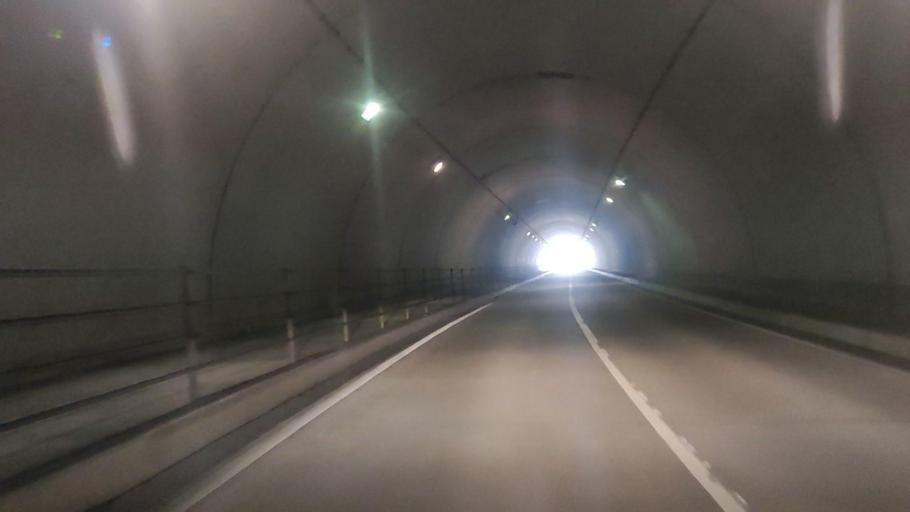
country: JP
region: Oita
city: Saiki
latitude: 32.8057
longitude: 131.8969
